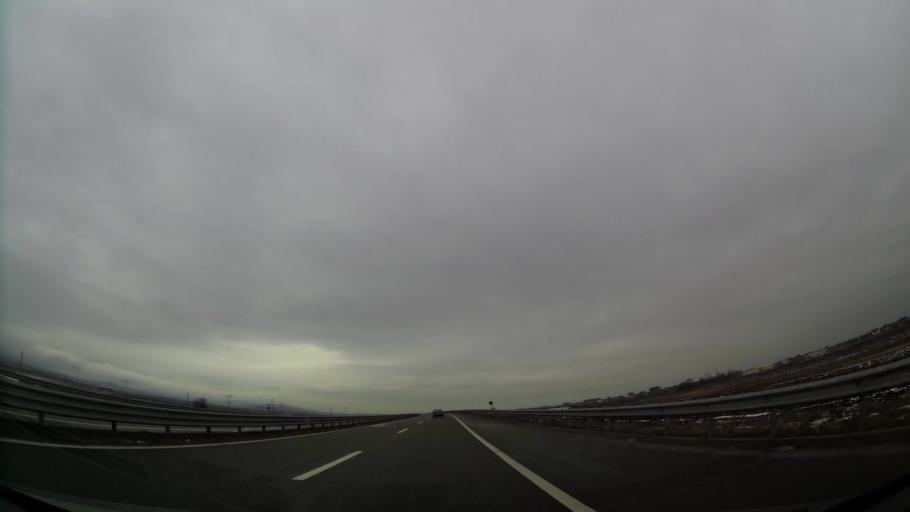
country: XK
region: Pristina
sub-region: Lipjan
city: Lipljan
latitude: 42.5254
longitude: 21.1666
